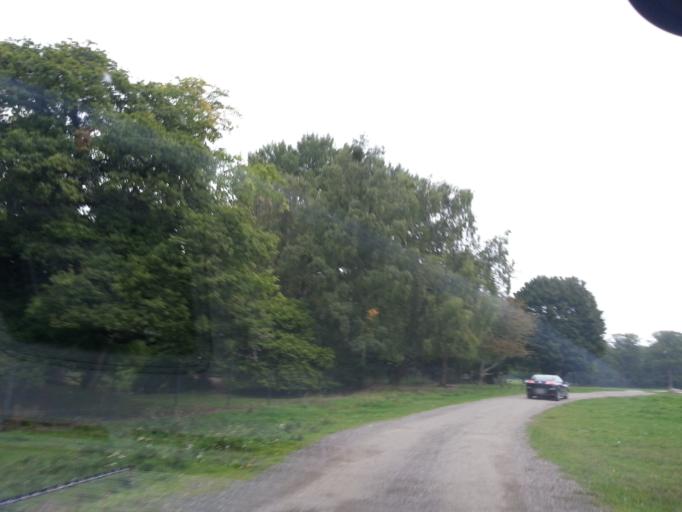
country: DK
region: Zealand
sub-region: Lolland Kommune
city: Maribo
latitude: 54.8237
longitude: 11.5113
